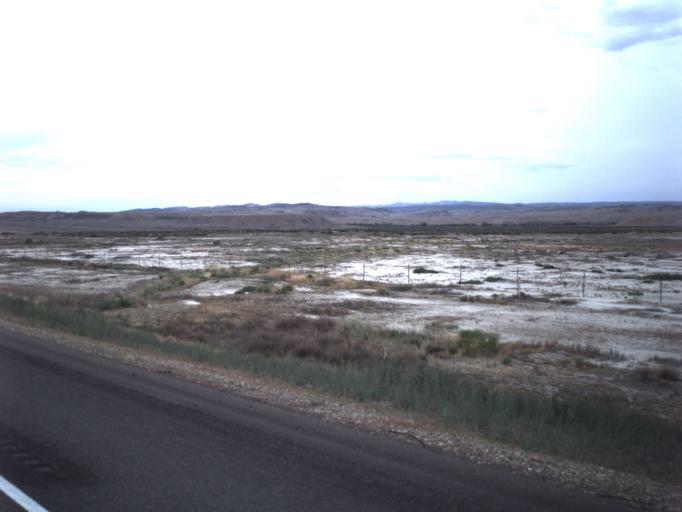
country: US
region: Utah
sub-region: Carbon County
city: East Carbon City
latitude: 39.3158
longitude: -110.3629
